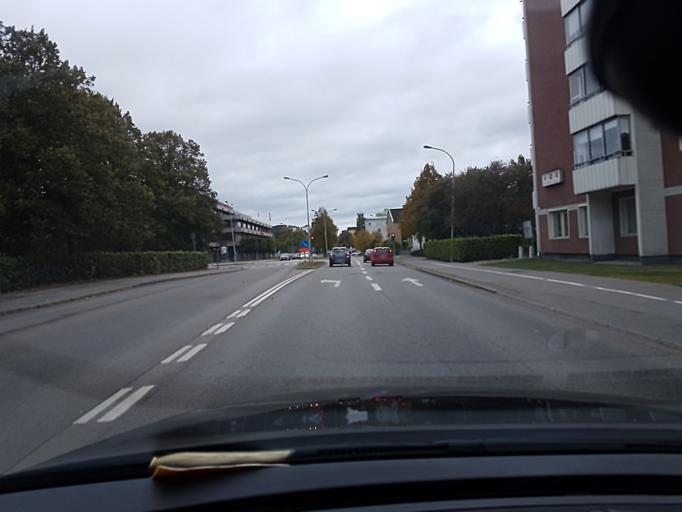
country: SE
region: Kronoberg
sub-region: Vaxjo Kommun
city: Vaexjoe
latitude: 56.8827
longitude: 14.8002
